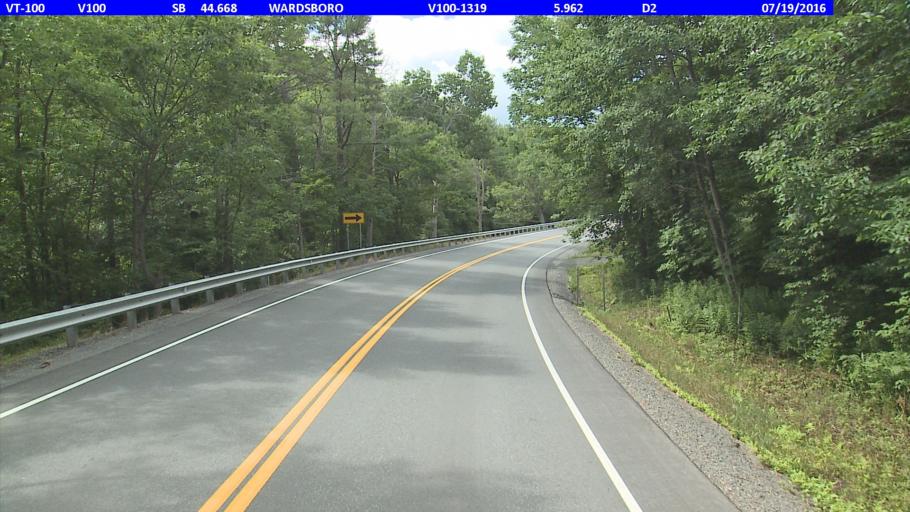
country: US
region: Vermont
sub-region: Windham County
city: Dover
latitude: 43.0846
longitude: -72.8662
